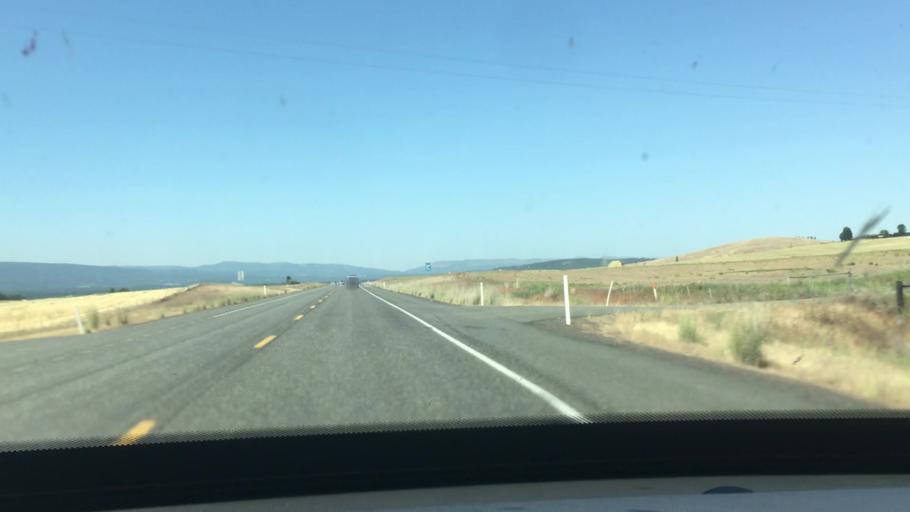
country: US
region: Washington
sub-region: Klickitat County
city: Goldendale
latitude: 45.7953
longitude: -120.8171
